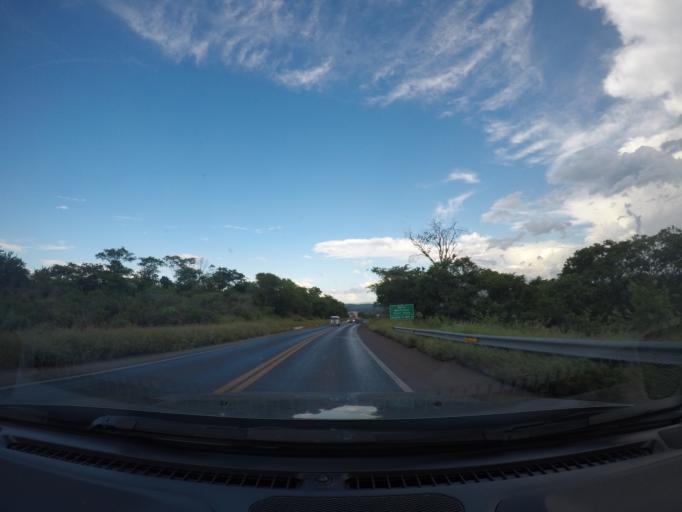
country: BR
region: Bahia
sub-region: Ibotirama
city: Ibotirama
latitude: -12.1305
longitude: -43.3450
